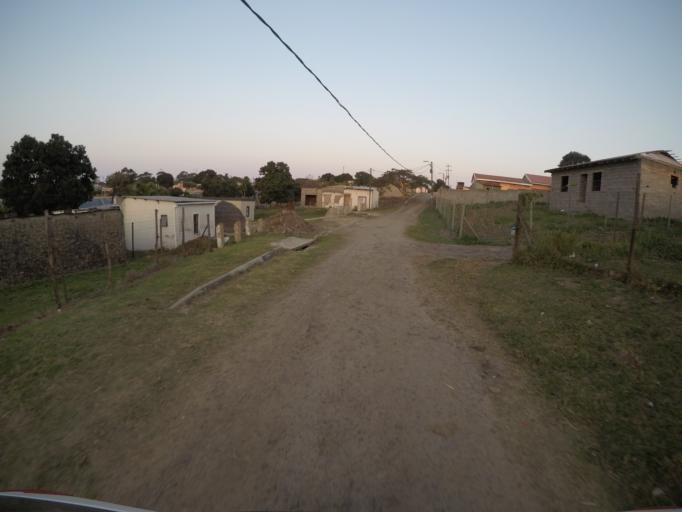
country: ZA
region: KwaZulu-Natal
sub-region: uThungulu District Municipality
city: Richards Bay
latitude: -28.7585
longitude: 32.1263
